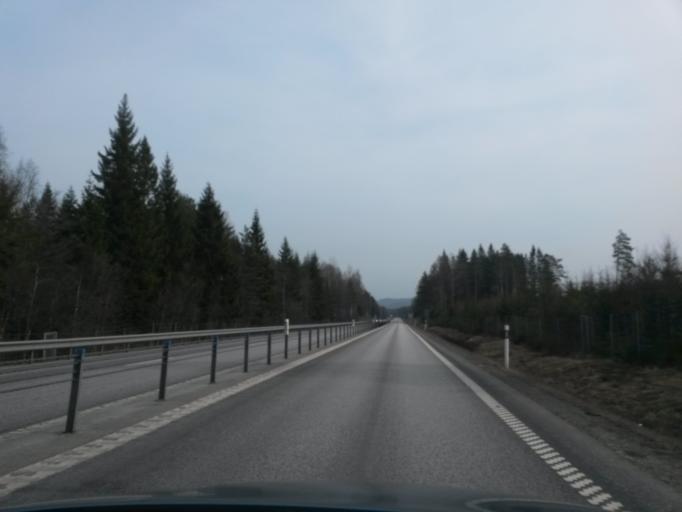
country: SE
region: Vaestra Goetaland
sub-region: Gullspangs Kommun
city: Anderstorp
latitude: 58.9161
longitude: 14.3884
